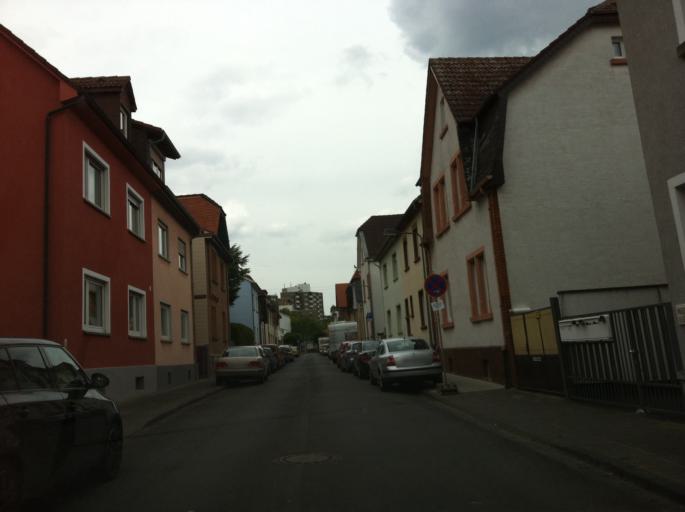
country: DE
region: Hesse
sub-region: Regierungsbezirk Darmstadt
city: Eschborn
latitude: 50.1219
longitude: 8.5646
